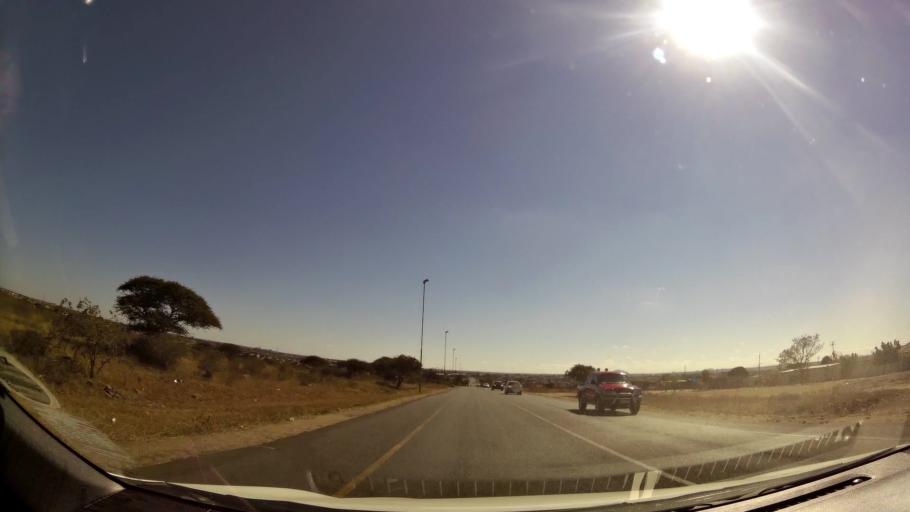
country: ZA
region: Limpopo
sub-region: Capricorn District Municipality
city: Polokwane
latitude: -23.8586
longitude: 29.4100
